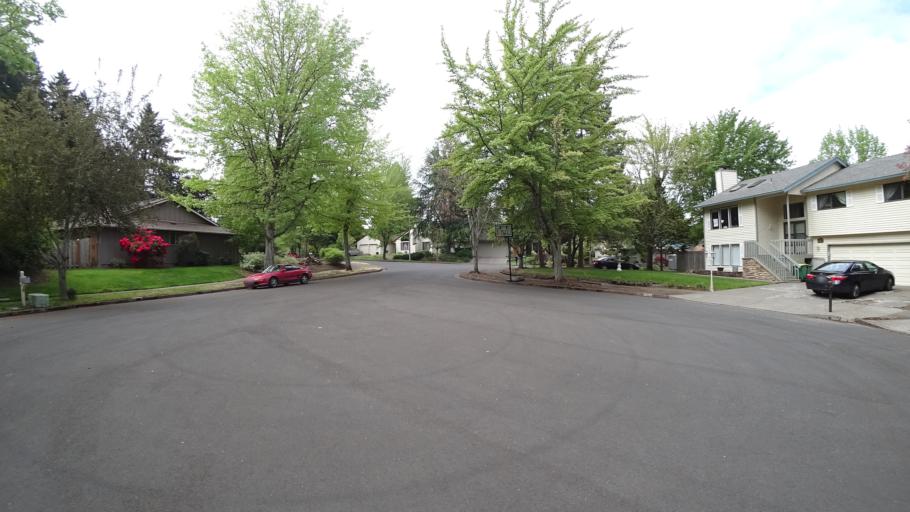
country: US
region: Oregon
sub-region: Washington County
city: Beaverton
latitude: 45.4734
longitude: -122.8126
